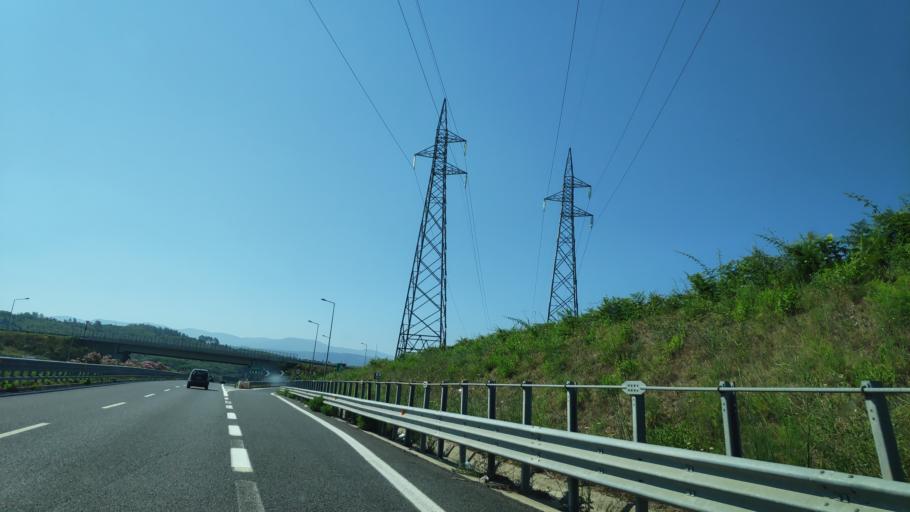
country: IT
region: Calabria
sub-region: Provincia di Reggio Calabria
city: Ceramida-Pellegrina
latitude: 38.3143
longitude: 15.8428
